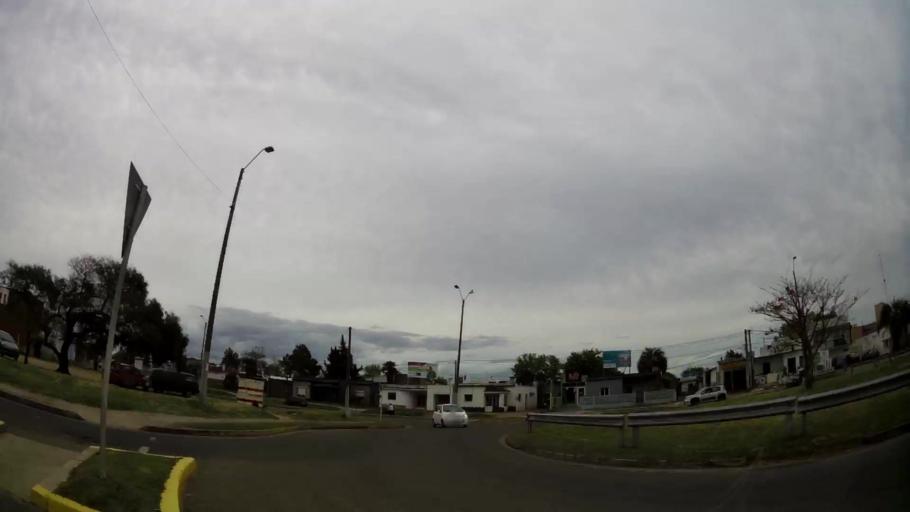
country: UY
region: Maldonado
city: Maldonado
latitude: -34.9020
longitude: -54.9636
